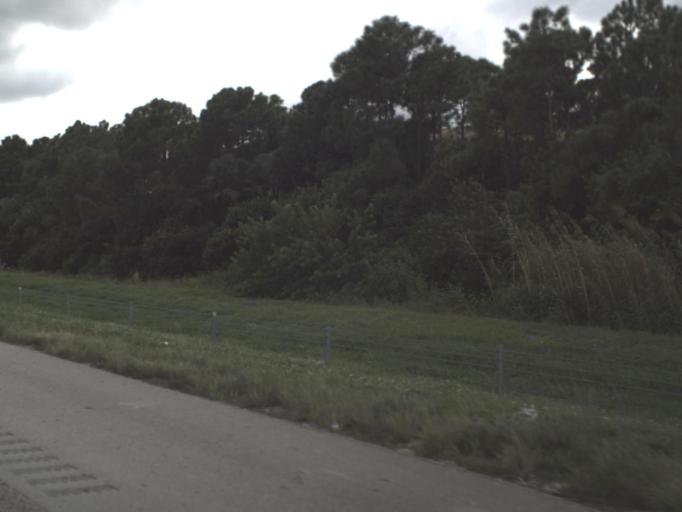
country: US
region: Florida
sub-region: Palm Beach County
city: Palm Beach Gardens
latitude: 26.7855
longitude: -80.1323
